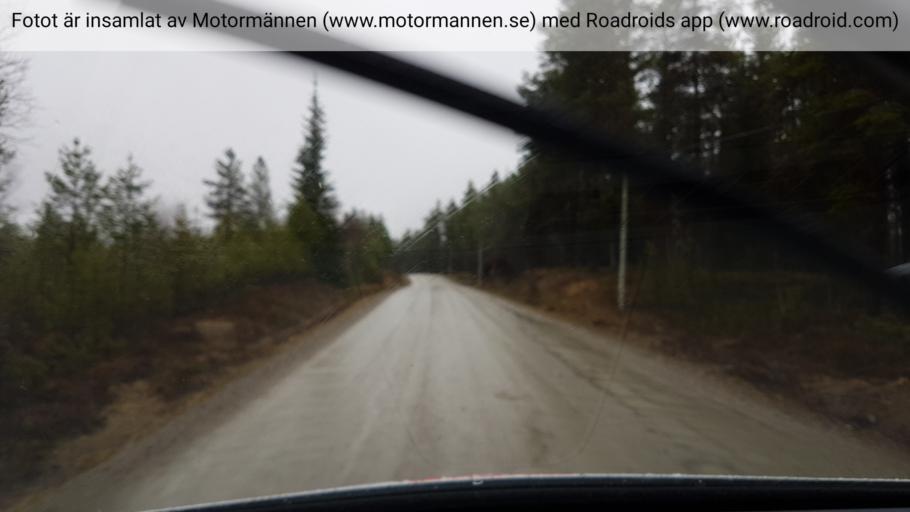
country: SE
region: Jaemtland
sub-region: Are Kommun
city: Jarpen
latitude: 62.5154
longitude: 13.4879
